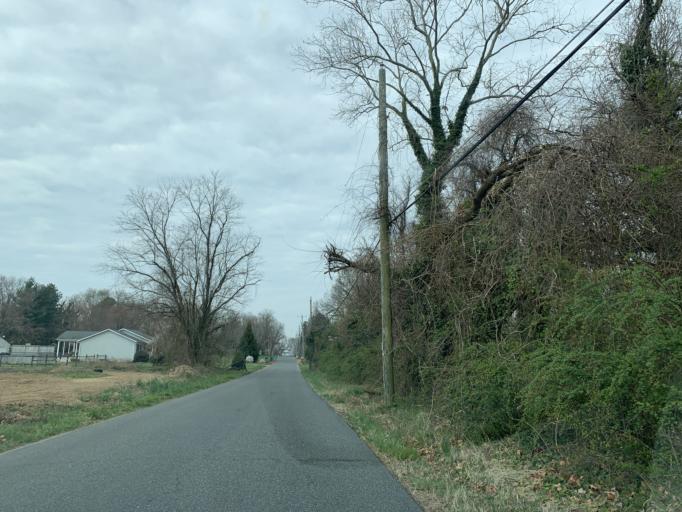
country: US
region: Maryland
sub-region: Baltimore County
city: Edgemere
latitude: 39.2573
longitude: -76.4322
